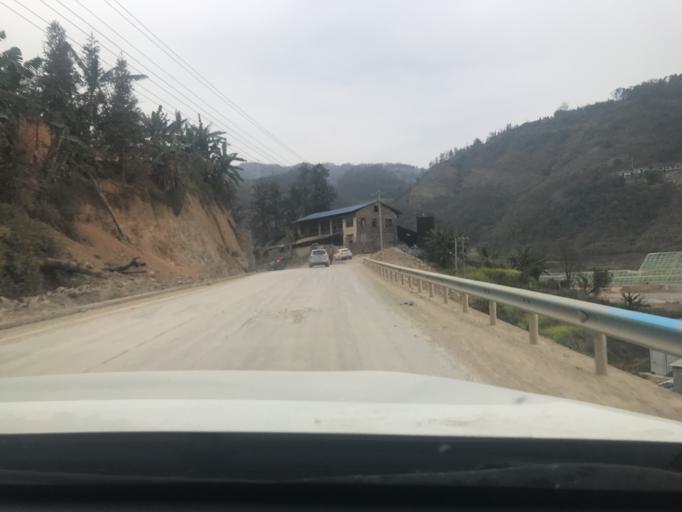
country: CN
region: Guangxi Zhuangzu Zizhiqu
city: Xinzhou
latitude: 25.0096
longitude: 105.8496
